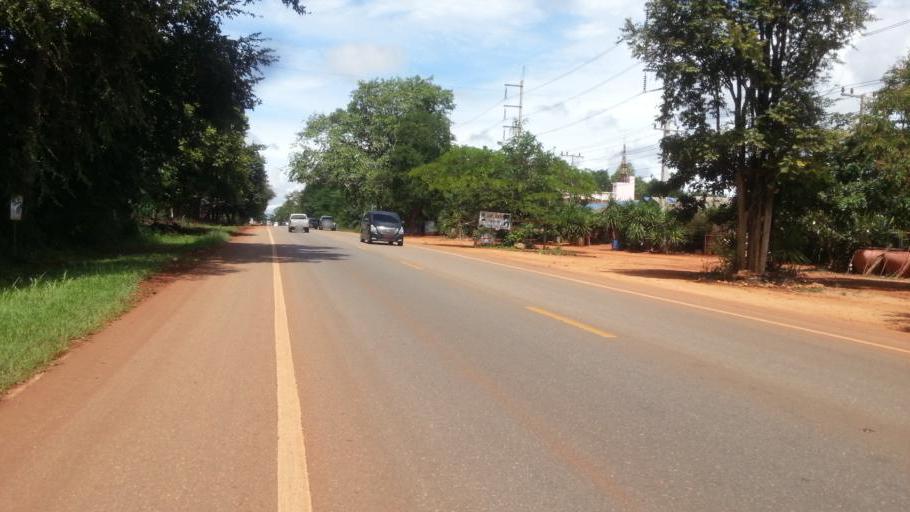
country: TH
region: Kanchanaburi
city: Sai Yok
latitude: 14.1197
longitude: 99.1831
